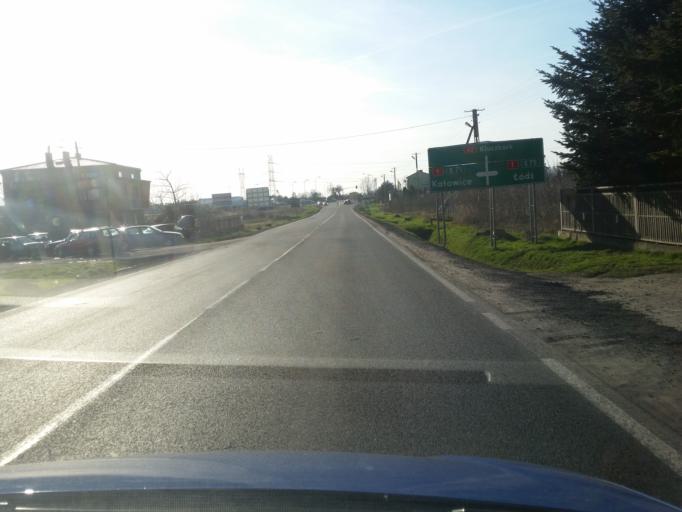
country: PL
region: Lodz Voivodeship
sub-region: Powiat radomszczanski
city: Radomsko
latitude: 51.0794
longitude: 19.3768
